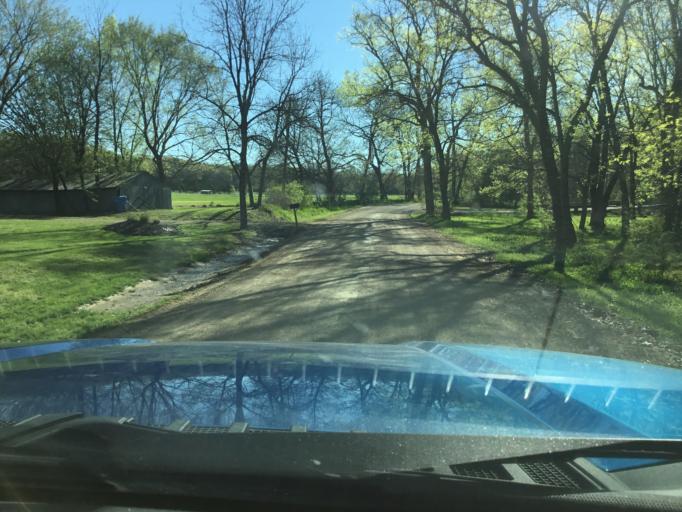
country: US
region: Kansas
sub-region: Douglas County
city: Lawrence
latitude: 38.9935
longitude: -95.3280
